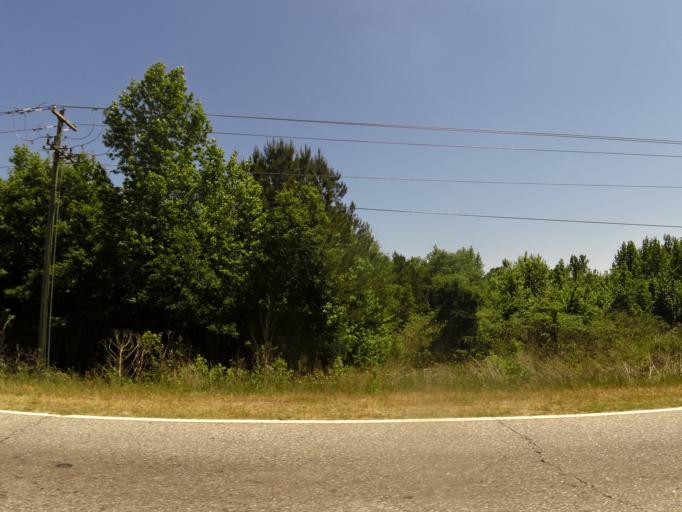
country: US
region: South Carolina
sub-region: Aiken County
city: Burnettown
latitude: 33.5110
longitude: -81.8686
